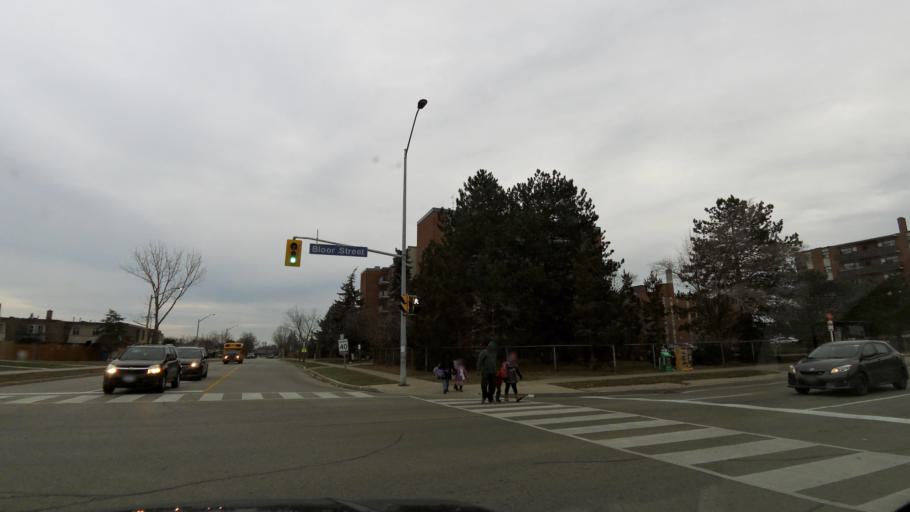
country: CA
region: Ontario
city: Etobicoke
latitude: 43.6192
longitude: -79.5921
